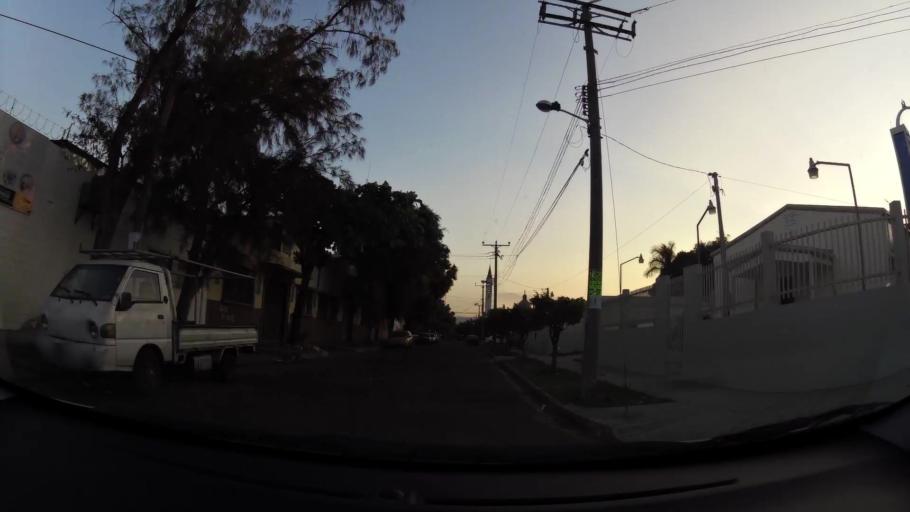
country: SV
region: San Salvador
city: Cuscatancingo
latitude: 13.7158
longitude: -89.1916
